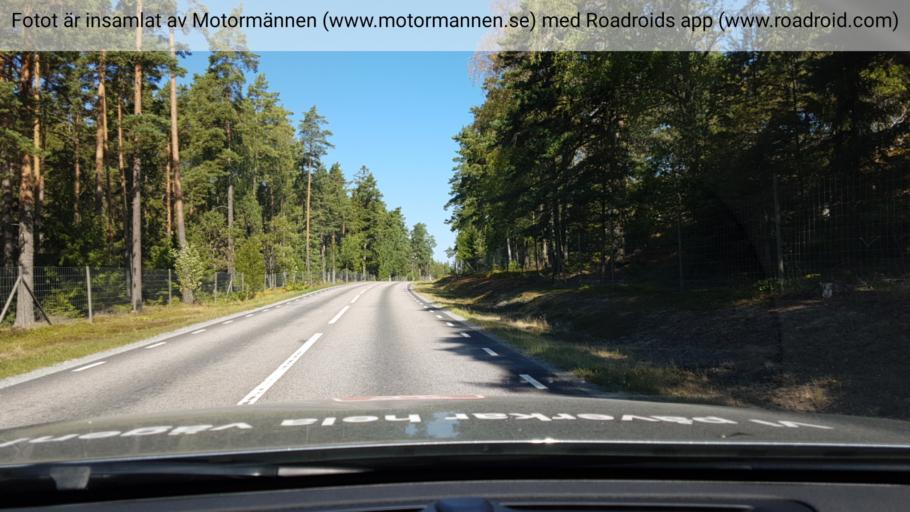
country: SE
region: Stockholm
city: Stenhamra
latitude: 59.3084
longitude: 17.6417
